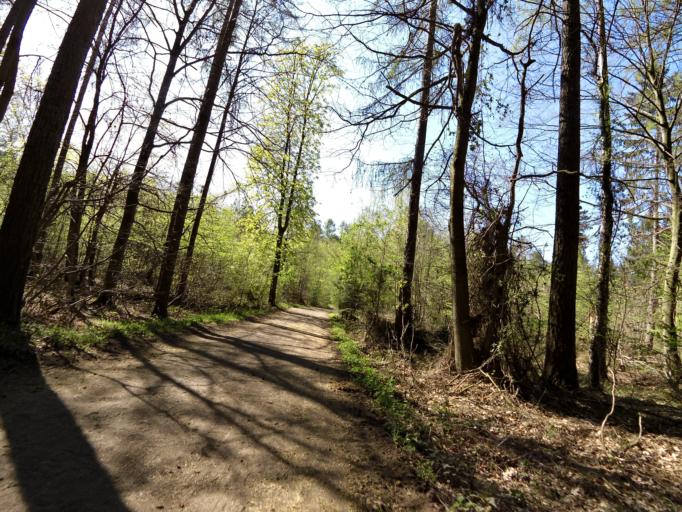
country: DE
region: North Rhine-Westphalia
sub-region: Regierungsbezirk Koln
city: Alfter
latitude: 50.6827
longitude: 6.9918
